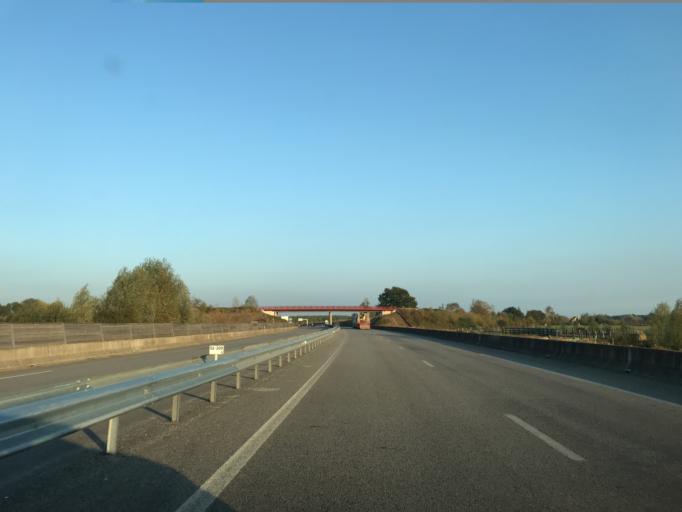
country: FR
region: Lower Normandy
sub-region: Departement de l'Orne
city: Valframbert
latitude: 48.4793
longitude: 0.2350
